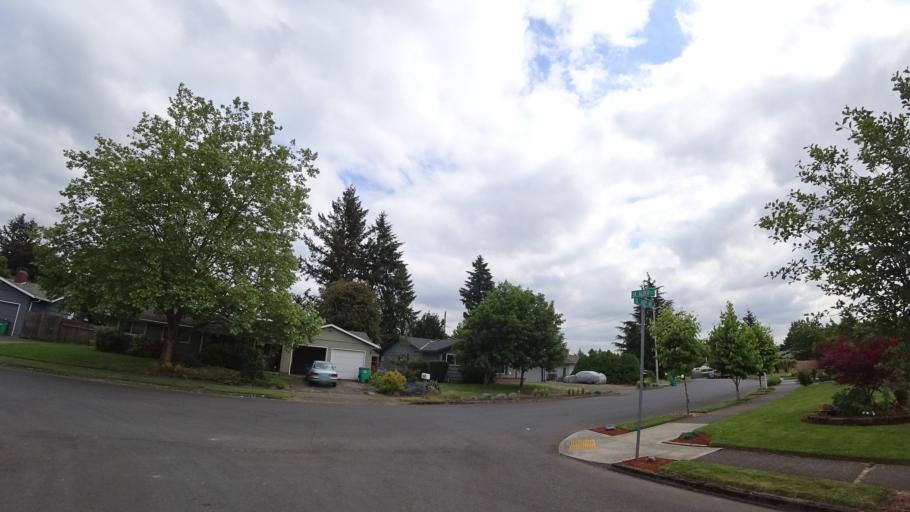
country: US
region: Oregon
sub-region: Multnomah County
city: Fairview
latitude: 45.5175
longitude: -122.4906
